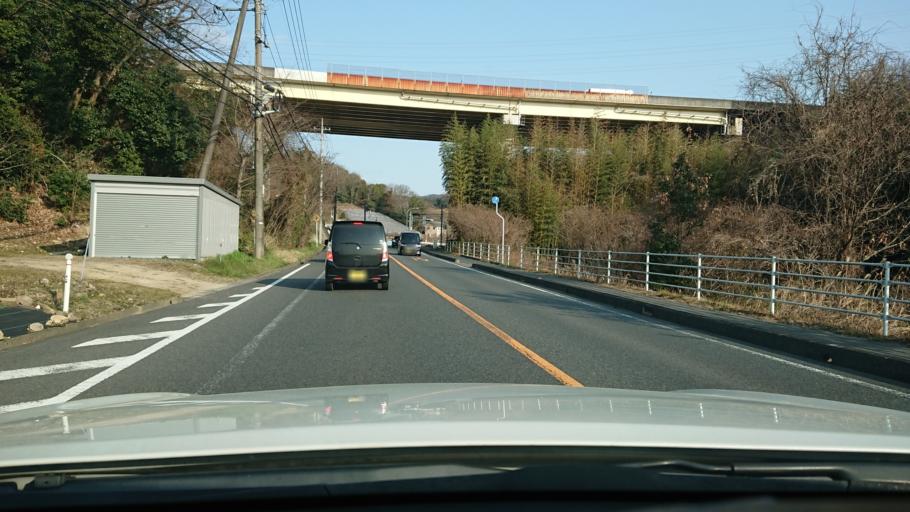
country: JP
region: Okayama
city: Kurashiki
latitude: 34.5819
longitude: 133.6833
